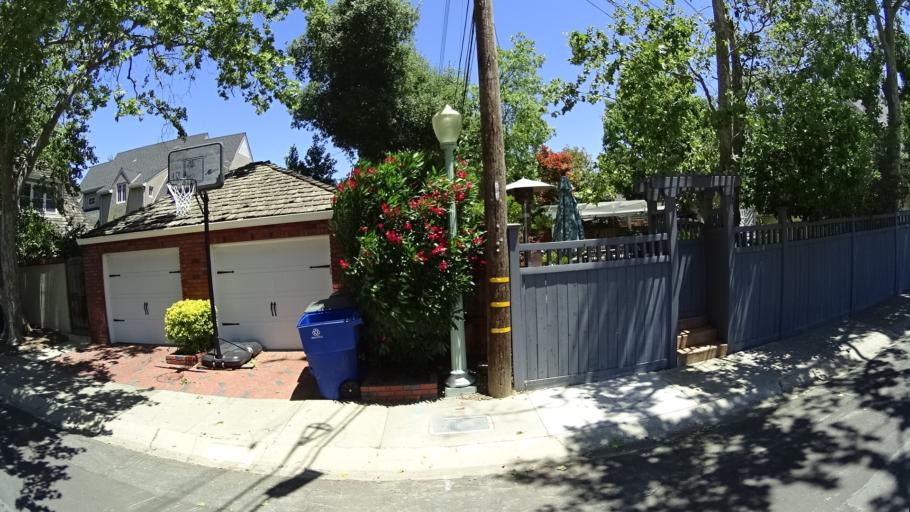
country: US
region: California
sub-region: Sacramento County
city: Sacramento
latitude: 38.5717
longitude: -121.4435
